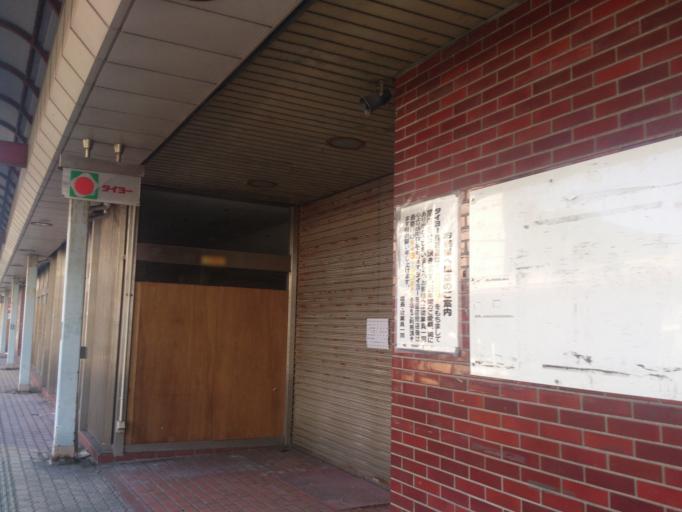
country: JP
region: Kagoshima
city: Kanoya
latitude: 31.3841
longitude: 130.8517
